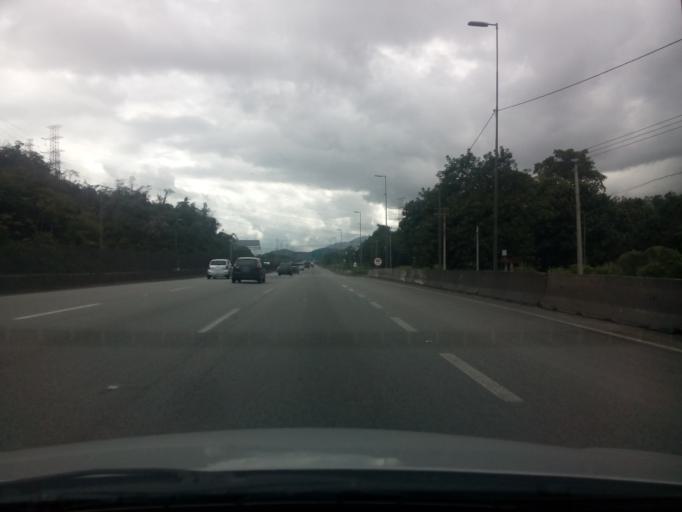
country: BR
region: Sao Paulo
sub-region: Cubatao
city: Cubatao
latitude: -23.8568
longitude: -46.4102
